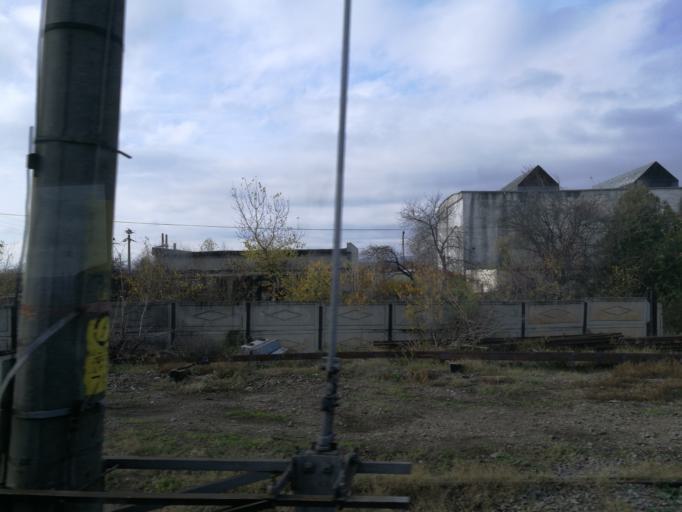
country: RO
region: Vrancea
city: Adjud
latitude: 46.0910
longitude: 27.1973
